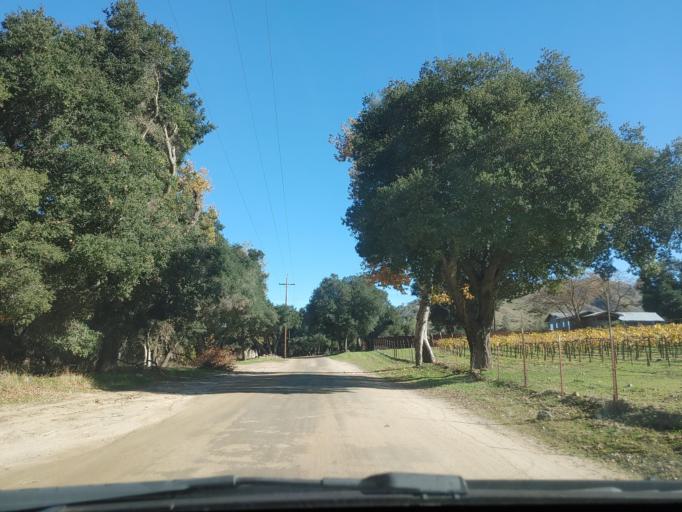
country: US
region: California
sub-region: San Benito County
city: Ridgemark
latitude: 36.6875
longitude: -121.3460
